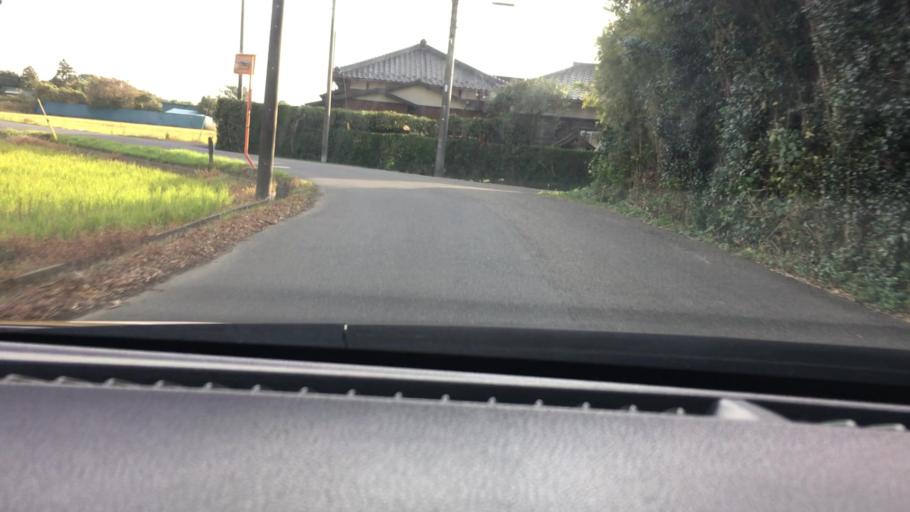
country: JP
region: Chiba
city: Kisarazu
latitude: 35.4005
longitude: 139.9564
